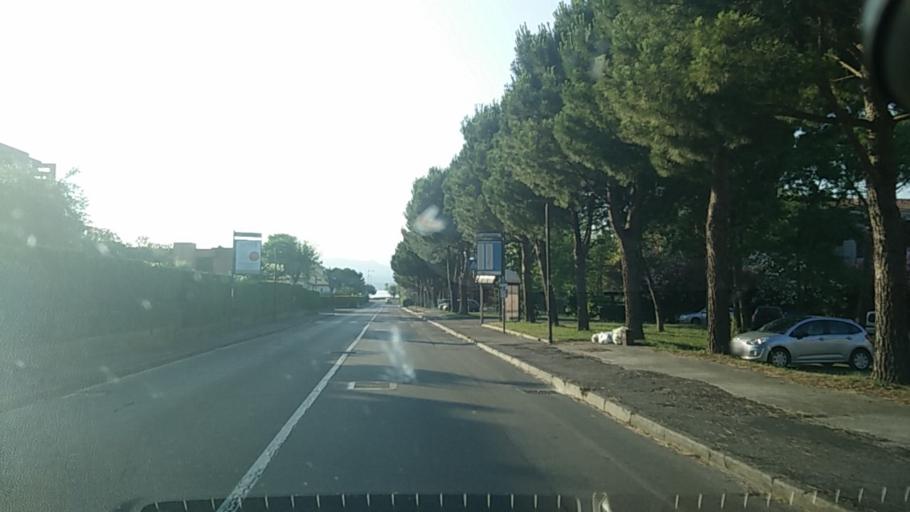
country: IT
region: Lombardy
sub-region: Provincia di Brescia
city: Desenzano del Garda
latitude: 45.4576
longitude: 10.5768
